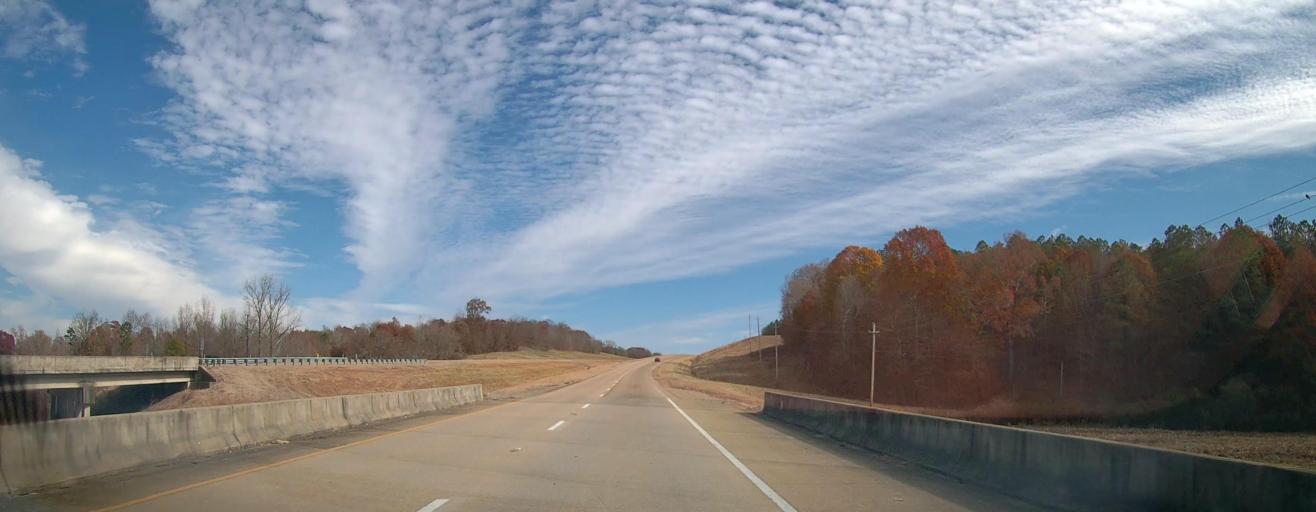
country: US
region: Mississippi
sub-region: Alcorn County
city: Corinth
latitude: 34.9323
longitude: -88.6524
